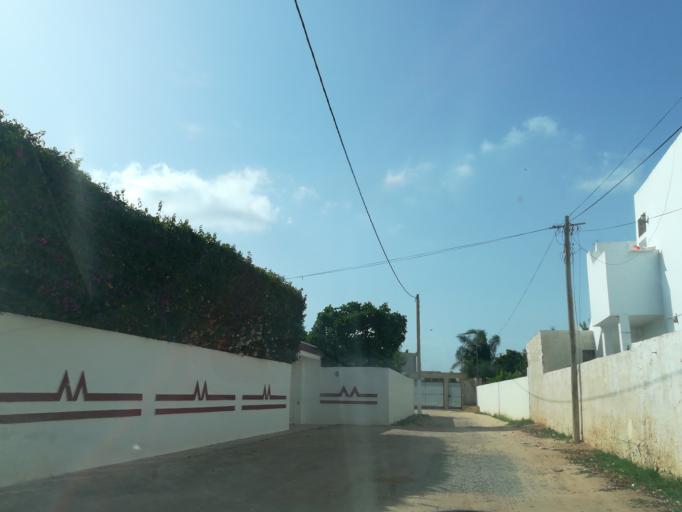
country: TN
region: Safaqis
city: Al Qarmadah
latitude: 34.8175
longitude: 10.7577
